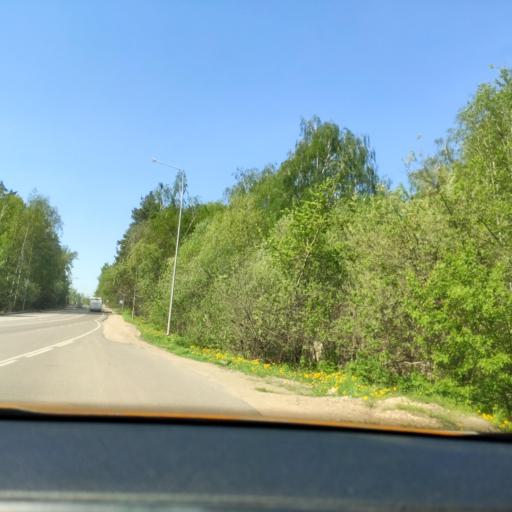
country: RU
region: Moskovskaya
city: Pavlovskaya Sloboda
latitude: 55.8135
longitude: 37.0484
